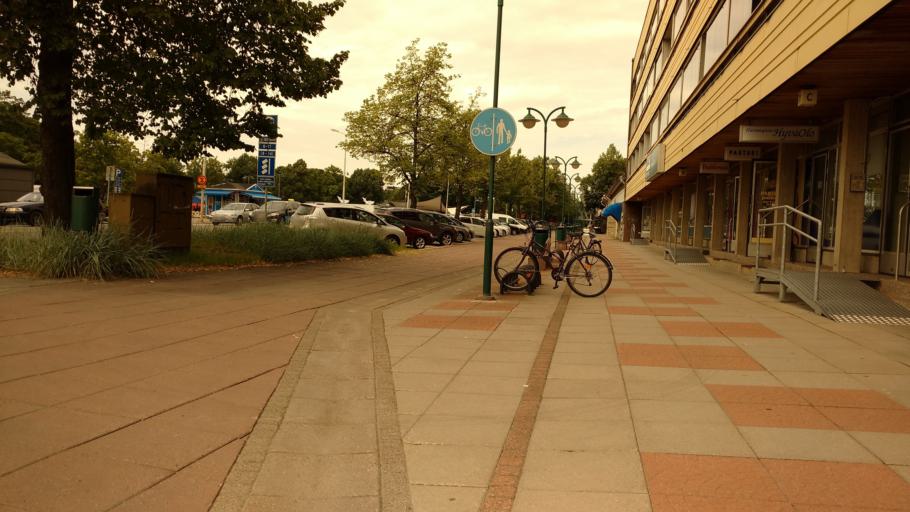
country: FI
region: Varsinais-Suomi
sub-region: Salo
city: Salo
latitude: 60.3837
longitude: 23.1301
